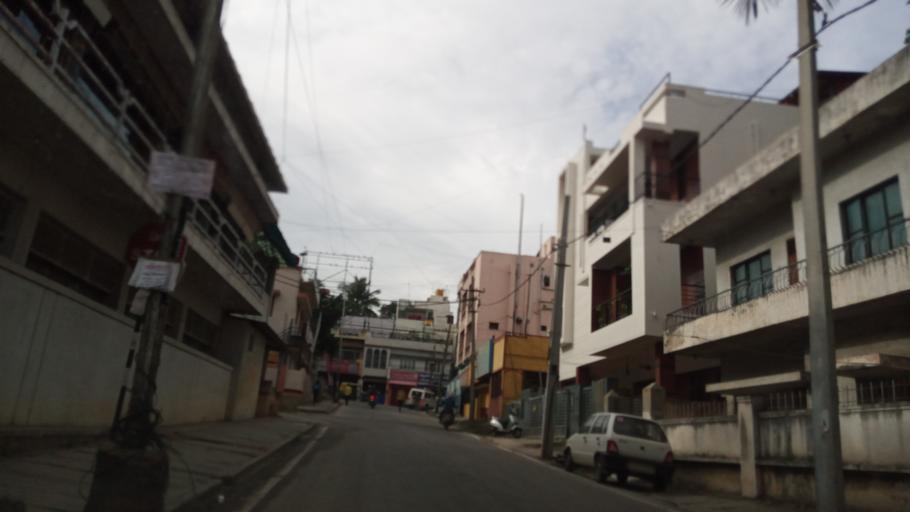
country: IN
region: Karnataka
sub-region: Bangalore Urban
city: Bangalore
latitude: 13.0092
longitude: 77.5437
